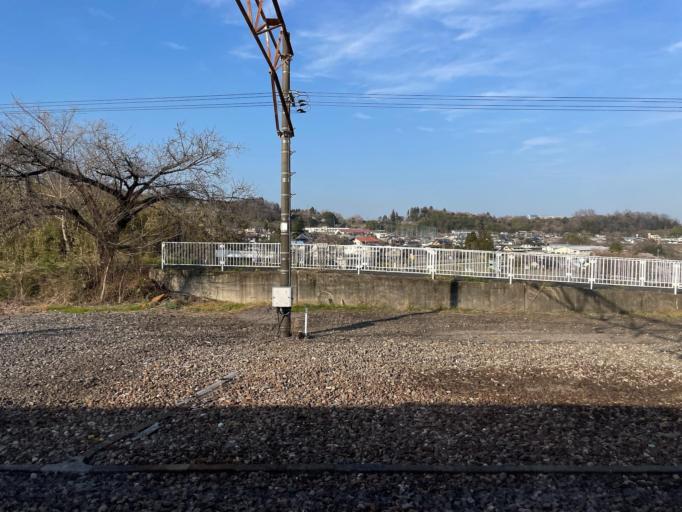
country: JP
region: Gunma
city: Annaka
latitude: 36.3083
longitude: 138.7991
